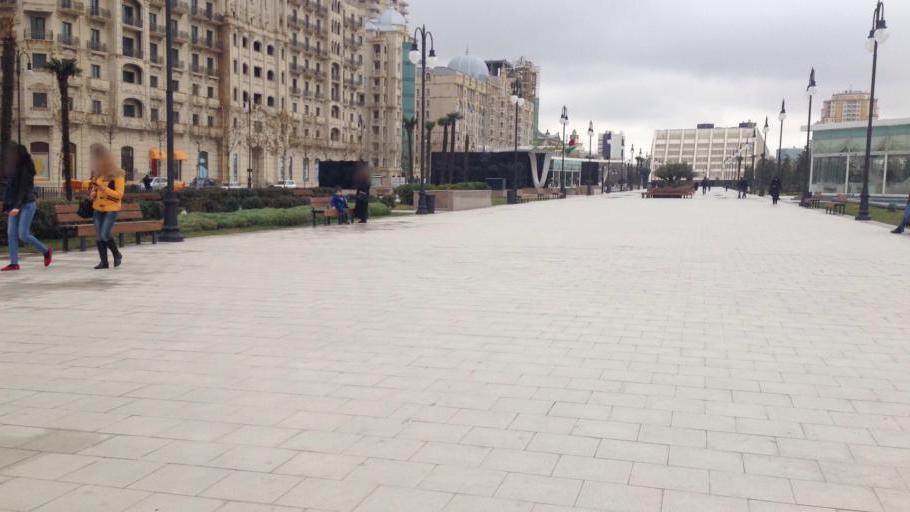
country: AZ
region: Baki
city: Badamdar
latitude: 40.3765
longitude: 49.8368
